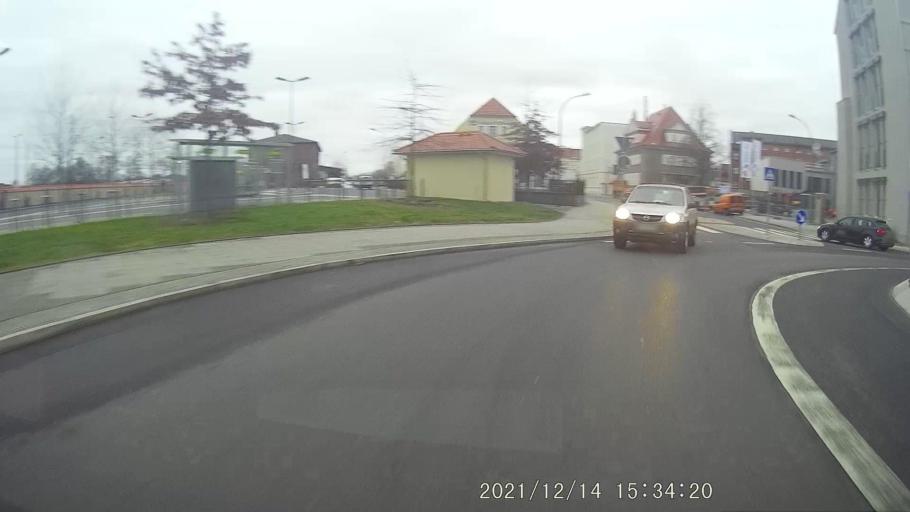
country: PL
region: Lower Silesian Voivodeship
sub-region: Powiat zgorzelecki
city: Lagow
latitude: 51.1871
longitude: 15.0281
